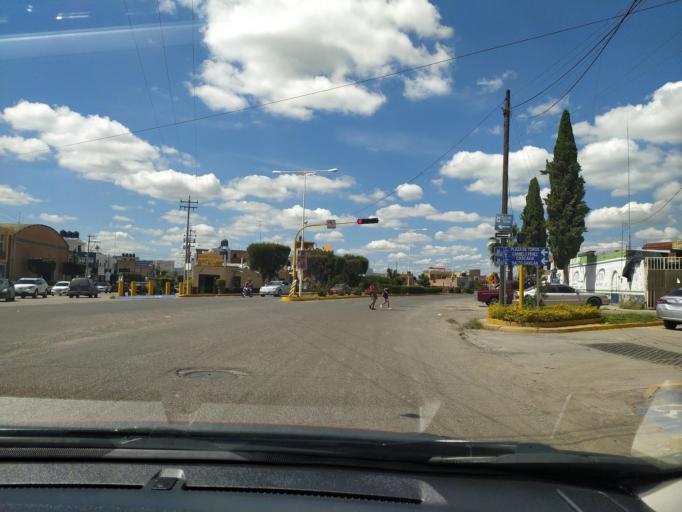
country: MX
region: Jalisco
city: San Miguel el Alto
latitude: 21.0303
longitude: -102.3926
